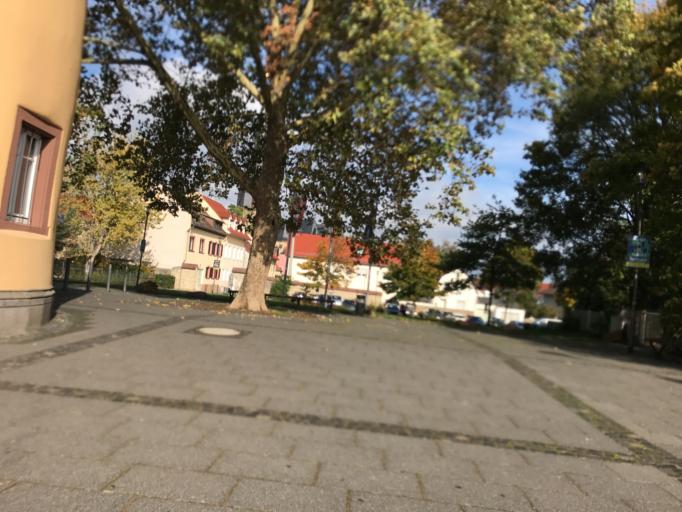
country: DE
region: Rheinland-Pfalz
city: Gau-Algesheim
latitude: 49.9546
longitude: 8.0168
